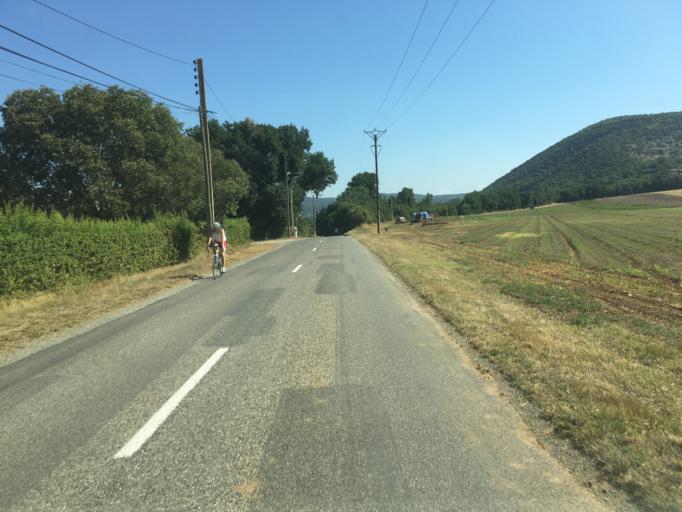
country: FR
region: Provence-Alpes-Cote d'Azur
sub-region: Departement des Alpes-de-Haute-Provence
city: Villeneuve
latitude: 43.8681
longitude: 5.8990
